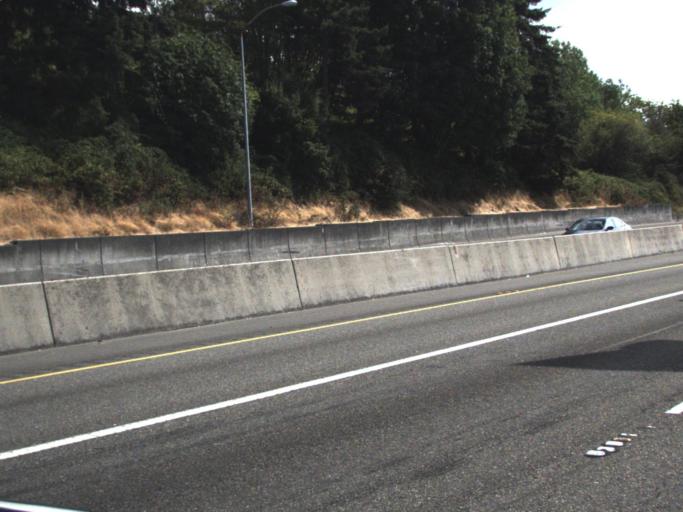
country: US
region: Washington
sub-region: King County
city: Renton
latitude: 47.4938
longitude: -122.1924
